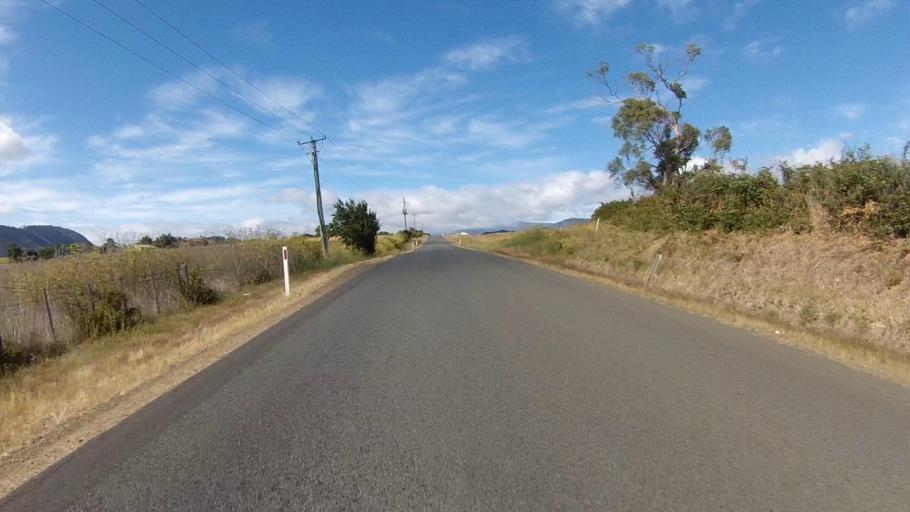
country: AU
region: Tasmania
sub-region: Brighton
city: Old Beach
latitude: -42.7590
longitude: 147.2799
